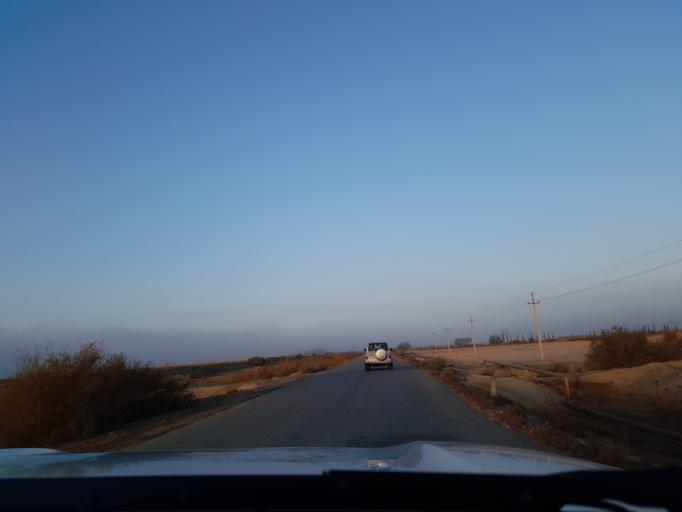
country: TM
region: Dasoguz
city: Koeneuergench
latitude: 41.8440
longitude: 58.6668
